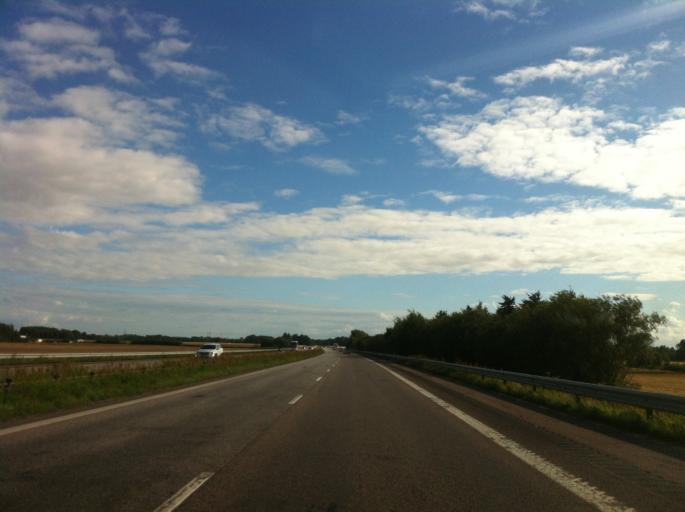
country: SE
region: Skane
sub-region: Bastads Kommun
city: Bastad
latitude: 56.3667
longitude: 12.9060
